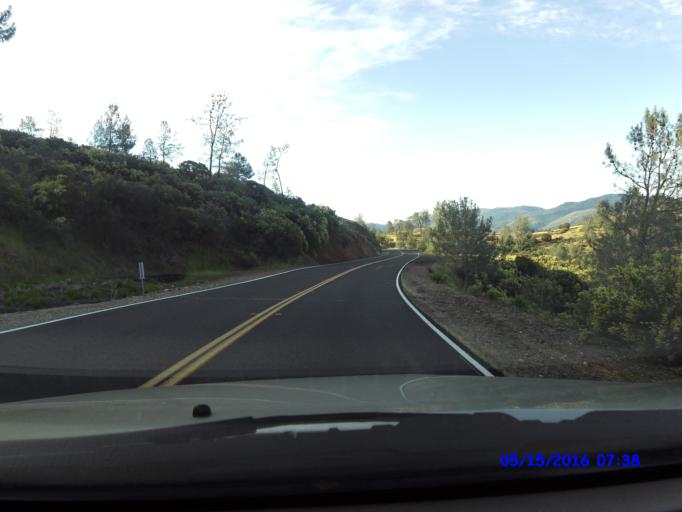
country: US
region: California
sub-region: Mariposa County
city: Mariposa
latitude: 37.6671
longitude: -120.1587
